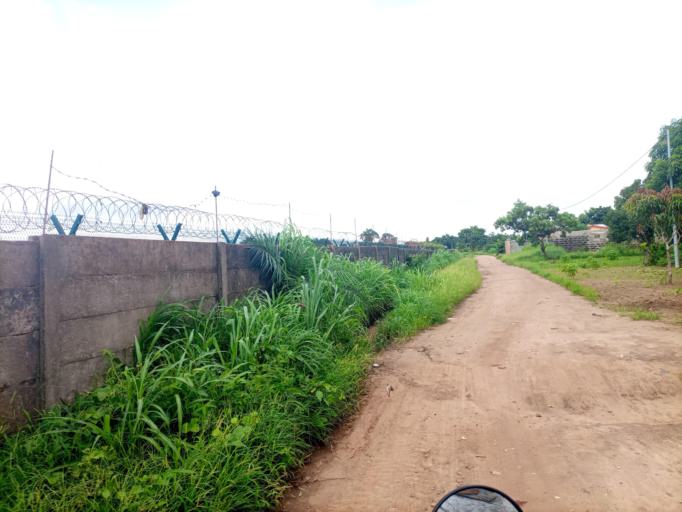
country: SL
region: Northern Province
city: Masoyila
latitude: 8.6105
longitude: -13.1790
